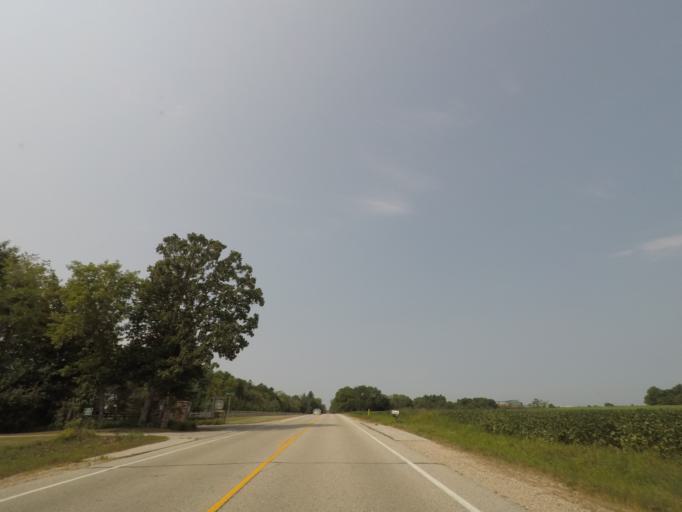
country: US
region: Wisconsin
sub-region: Waukesha County
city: Dousman
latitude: 43.0619
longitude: -88.4564
